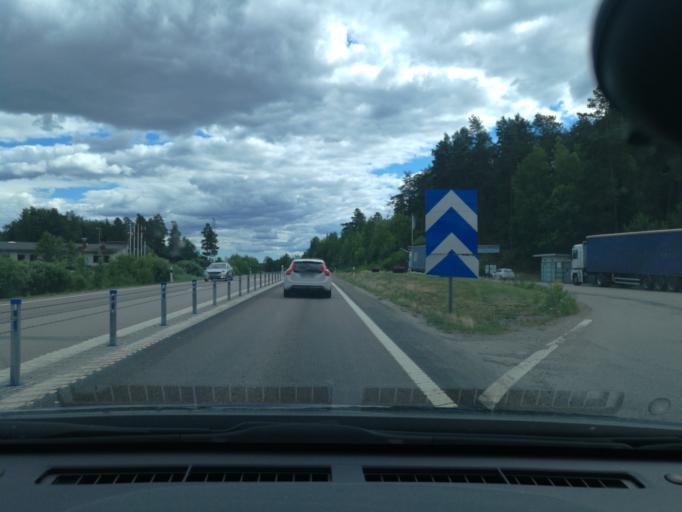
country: SE
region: OEstergoetland
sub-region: Soderkopings Kommun
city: Soederkoeping
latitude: 58.4973
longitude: 16.3016
